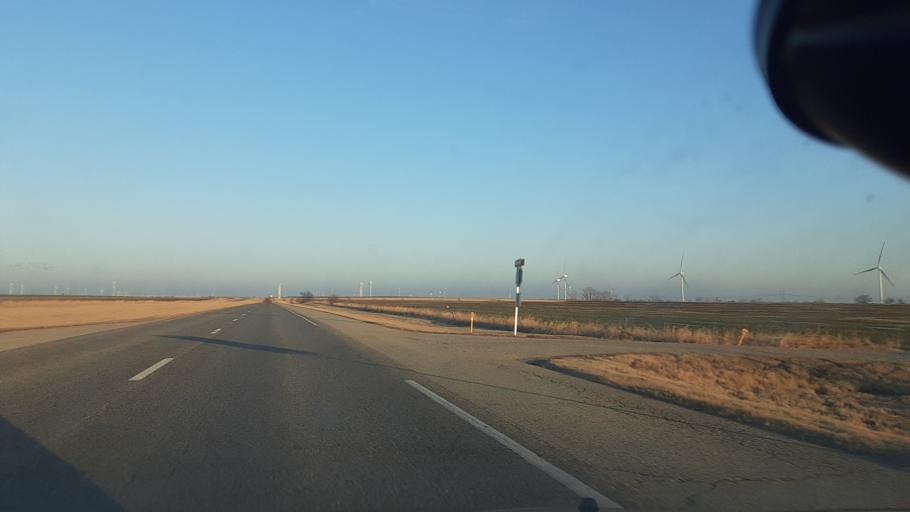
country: US
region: Oklahoma
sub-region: Noble County
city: Perry
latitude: 36.3975
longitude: -97.4972
